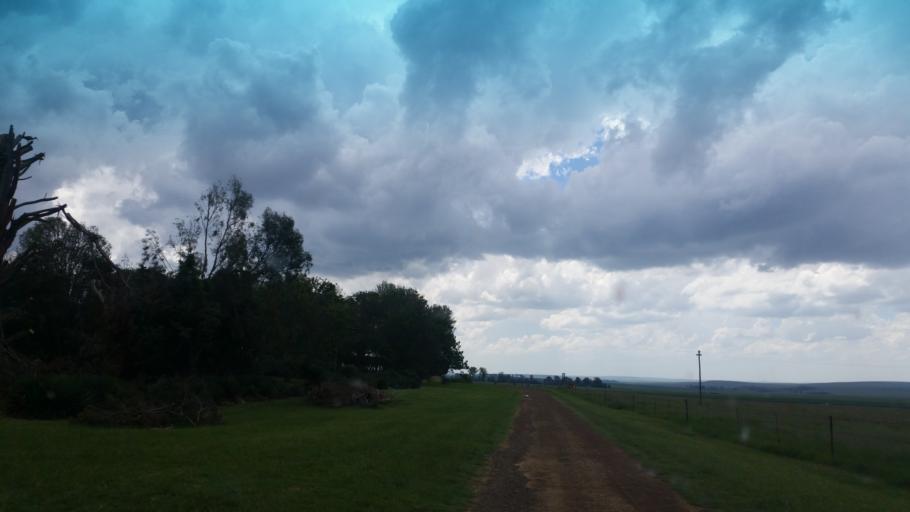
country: ZA
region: Orange Free State
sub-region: Thabo Mofutsanyana District Municipality
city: Harrismith
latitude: -28.1918
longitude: 29.0155
